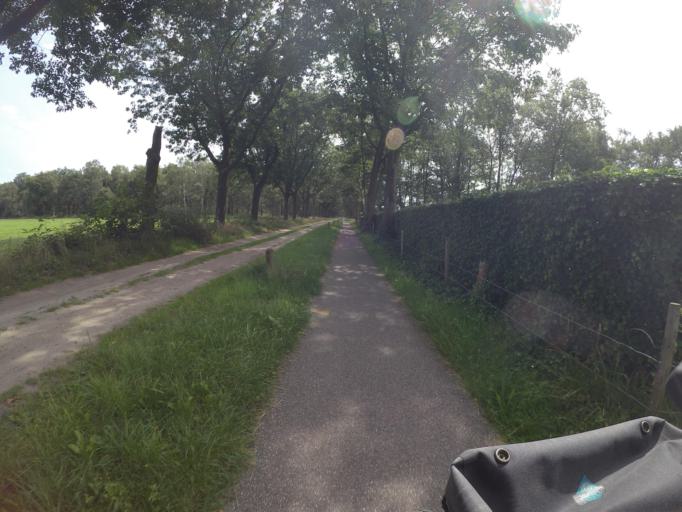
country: NL
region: North Brabant
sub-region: Bergeijk
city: Bergeyk
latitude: 51.3139
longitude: 5.3789
